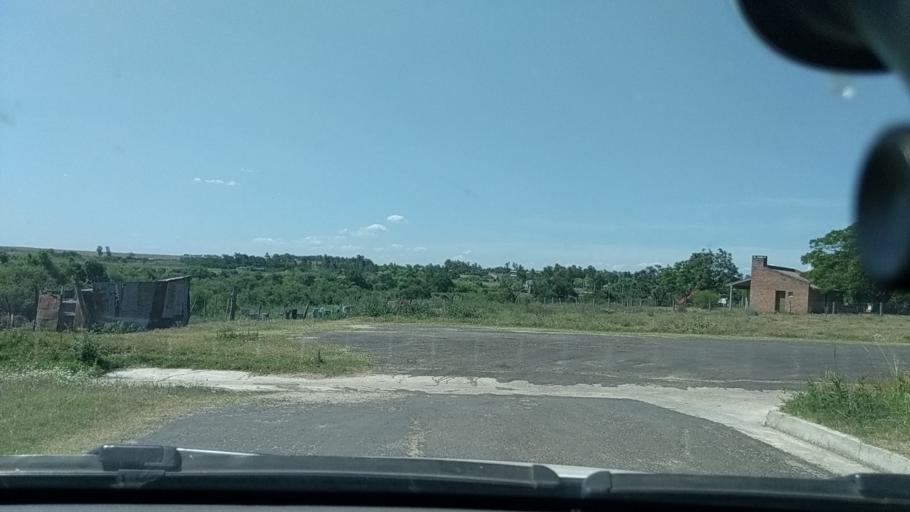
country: UY
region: Tacuarembo
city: Paso de los Toros
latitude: -32.8081
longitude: -56.5314
